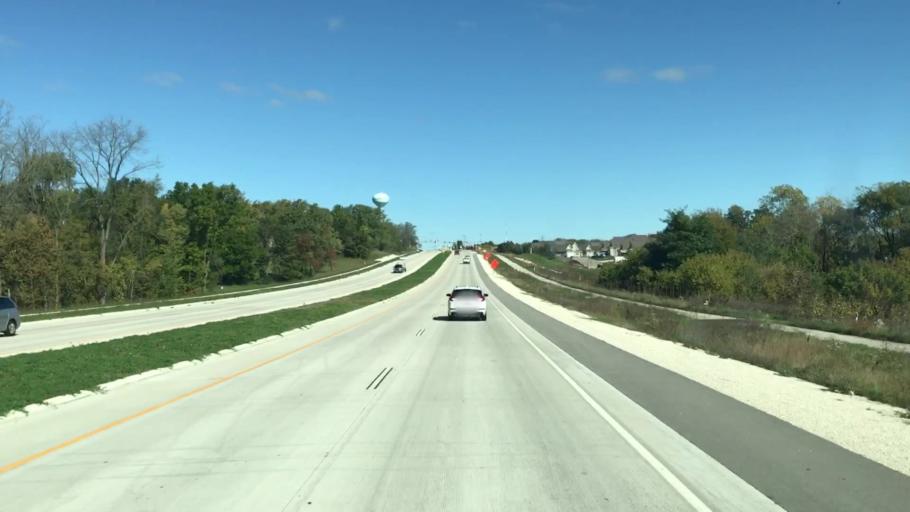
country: US
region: Wisconsin
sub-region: Waukesha County
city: Pewaukee
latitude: 43.0309
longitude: -88.2856
